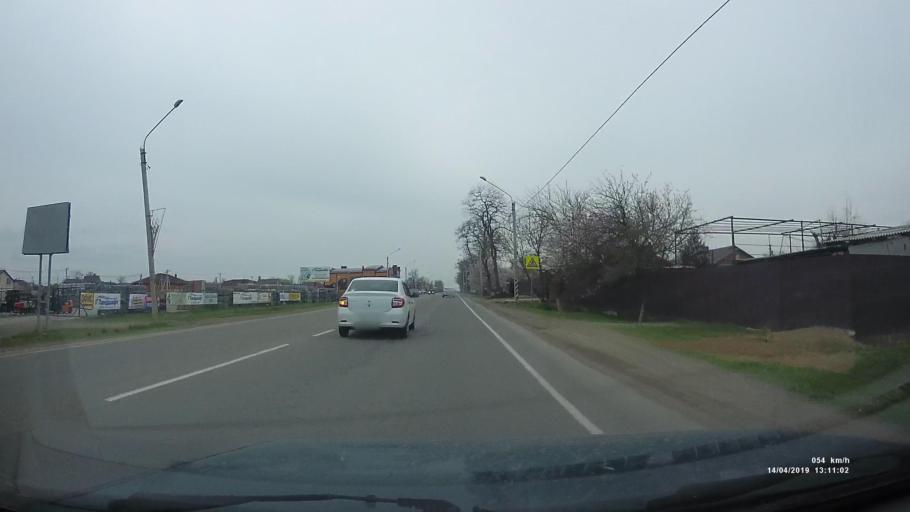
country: RU
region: Rostov
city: Kuleshovka
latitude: 47.1068
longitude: 39.6463
